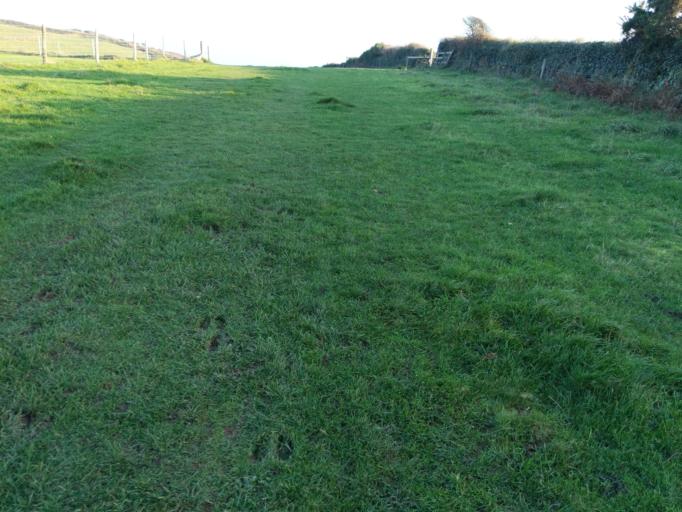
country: GB
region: England
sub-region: Cornwall
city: Fowey
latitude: 50.3262
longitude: -4.6251
